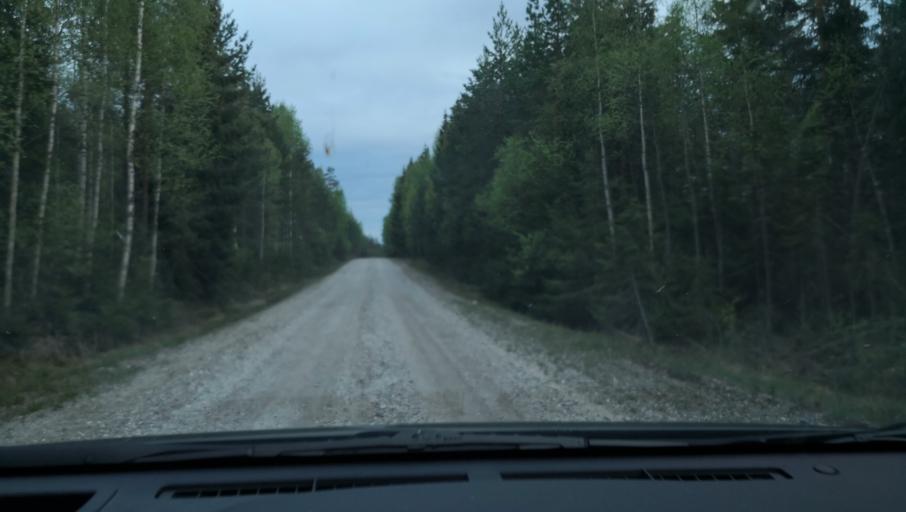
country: SE
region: Vaestmanland
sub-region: Skinnskattebergs Kommun
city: Skinnskatteberg
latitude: 59.7667
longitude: 15.4568
